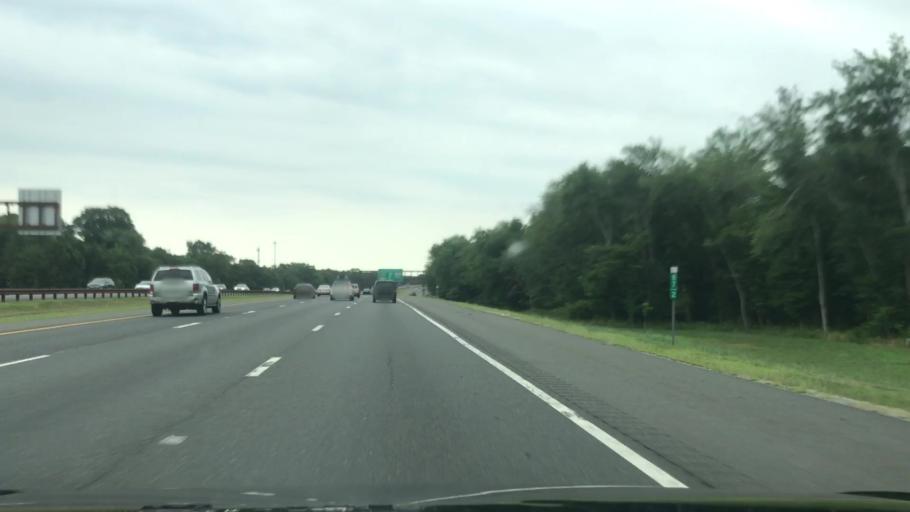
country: US
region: New Jersey
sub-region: Ocean County
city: Leisure Village
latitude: 40.0261
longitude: -74.1845
